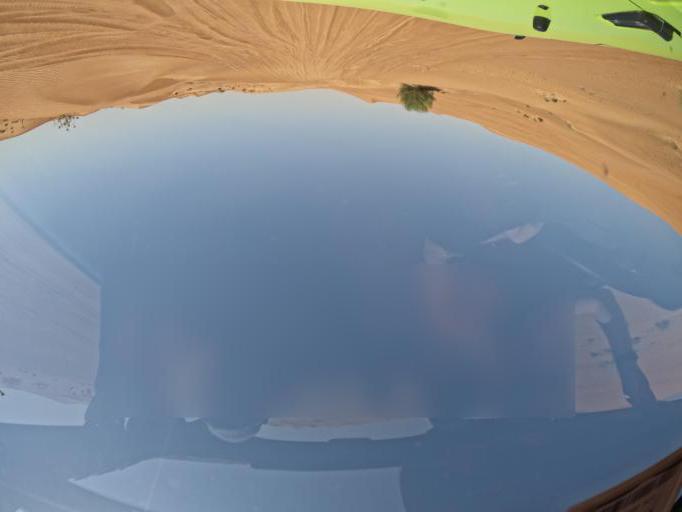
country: AE
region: Ash Shariqah
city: Adh Dhayd
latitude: 24.9804
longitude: 55.7219
